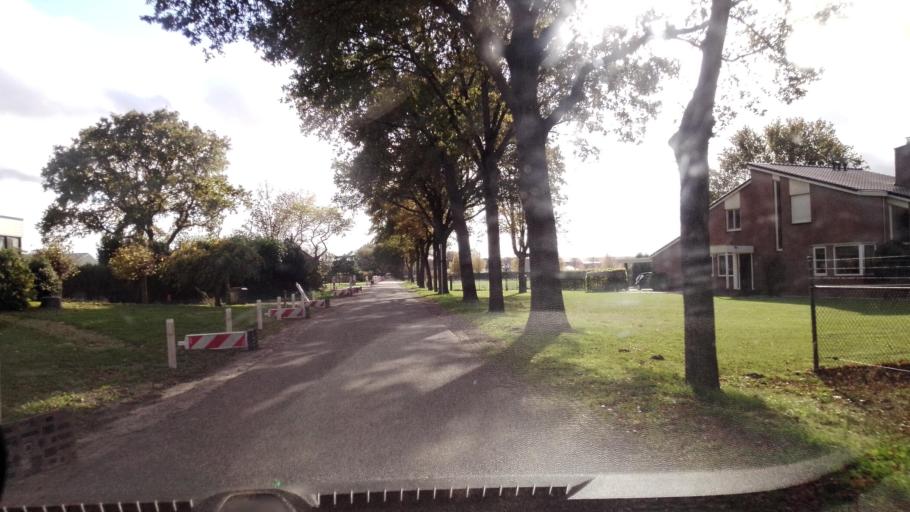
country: NL
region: Limburg
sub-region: Gemeente Venray
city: Venray
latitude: 51.4898
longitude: 5.9158
